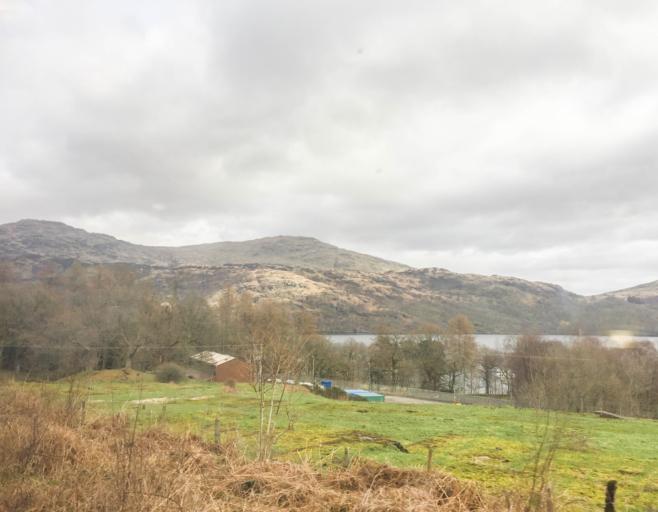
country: GB
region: Scotland
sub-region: Argyll and Bute
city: Garelochhead
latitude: 56.2482
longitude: -4.7159
